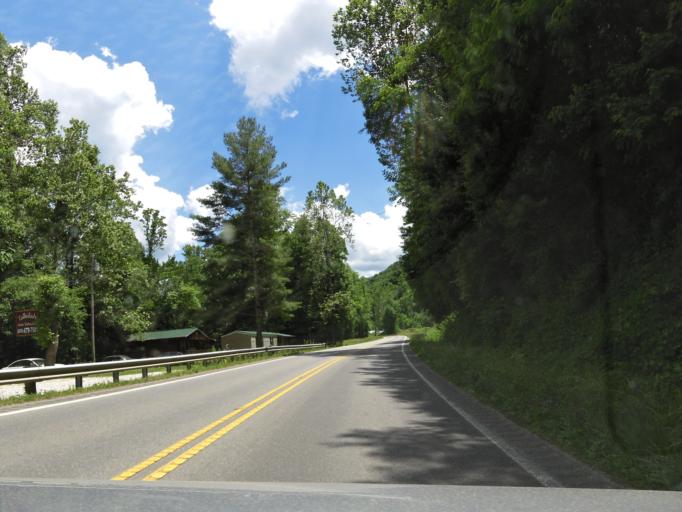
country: US
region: North Carolina
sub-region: Graham County
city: Robbinsville
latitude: 35.2866
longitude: -83.7670
